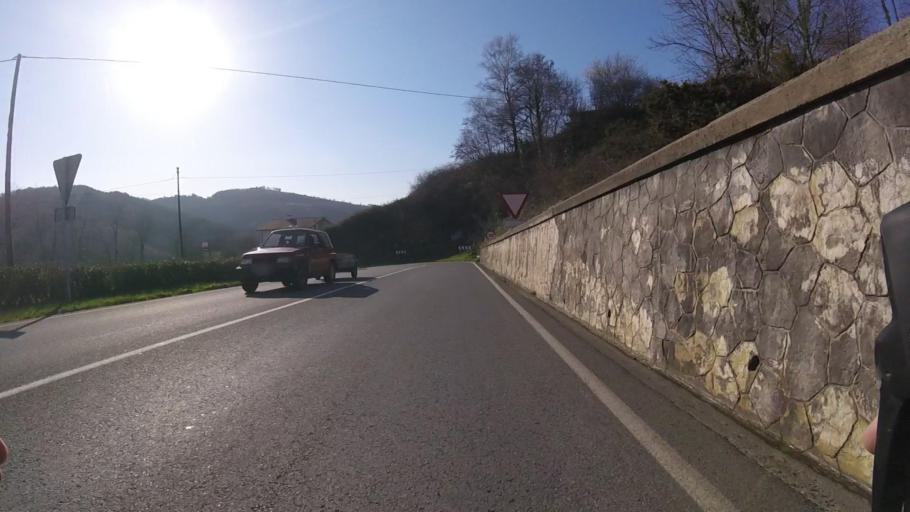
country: ES
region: Basque Country
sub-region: Provincia de Guipuzcoa
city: Errenteria
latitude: 43.2829
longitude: -1.9145
